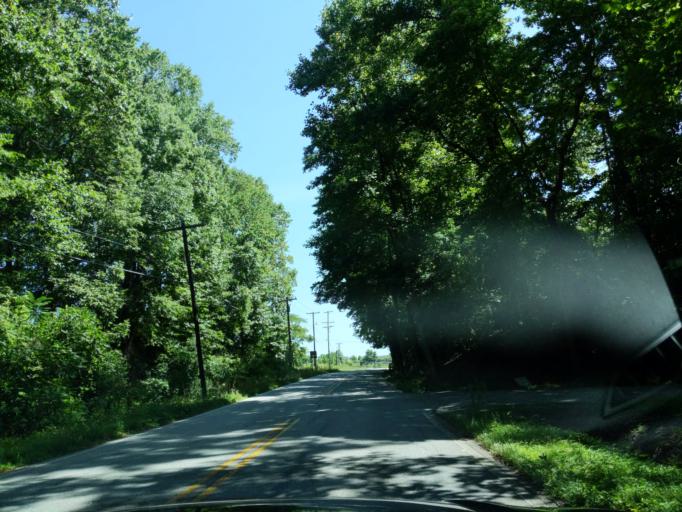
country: US
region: South Carolina
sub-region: Greenville County
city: Taylors
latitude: 34.9324
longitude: -82.2831
